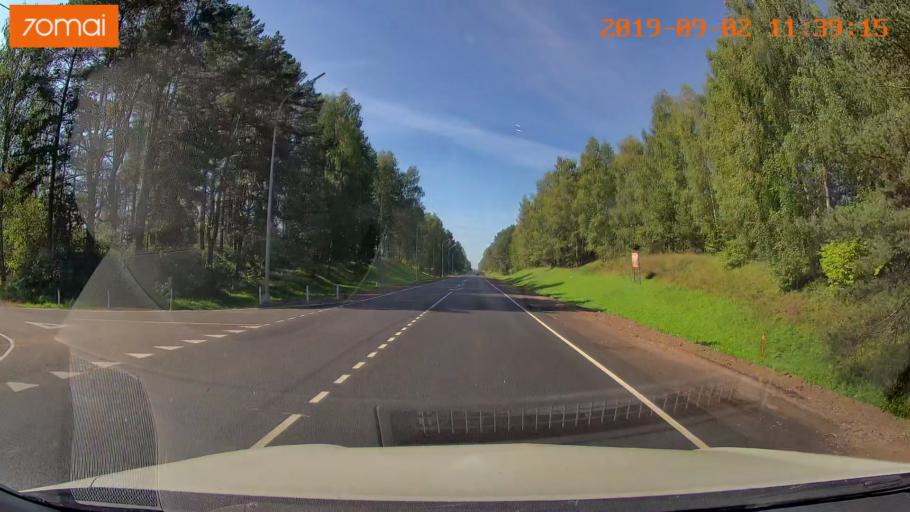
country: RU
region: Smolensk
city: Oster
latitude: 53.9091
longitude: 32.7266
